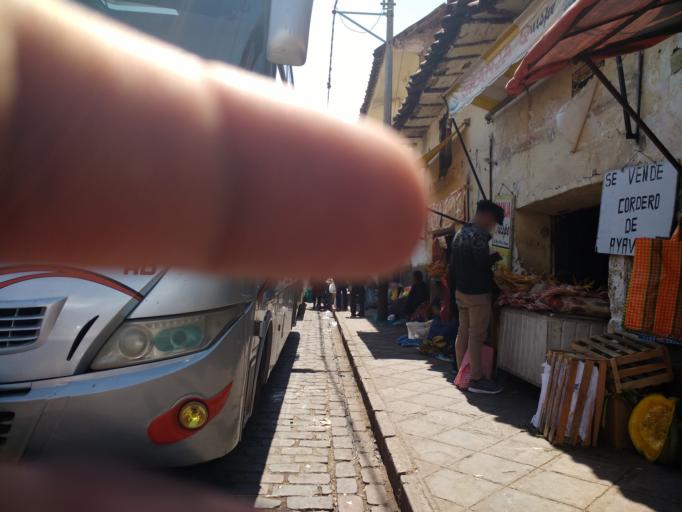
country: PE
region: Cusco
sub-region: Provincia de Cusco
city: Cusco
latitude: -13.5226
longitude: -71.9827
